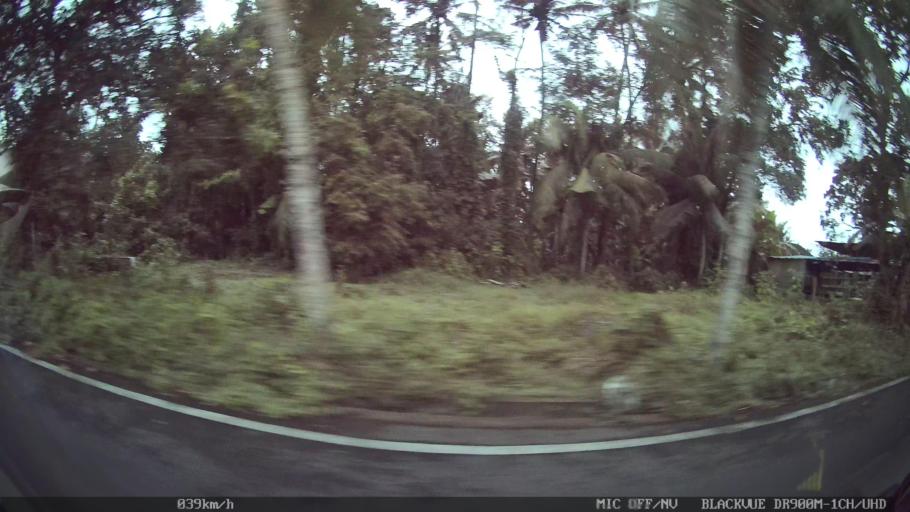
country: ID
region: Bali
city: Banjar Mambalkajanan
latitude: -8.5599
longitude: 115.2172
